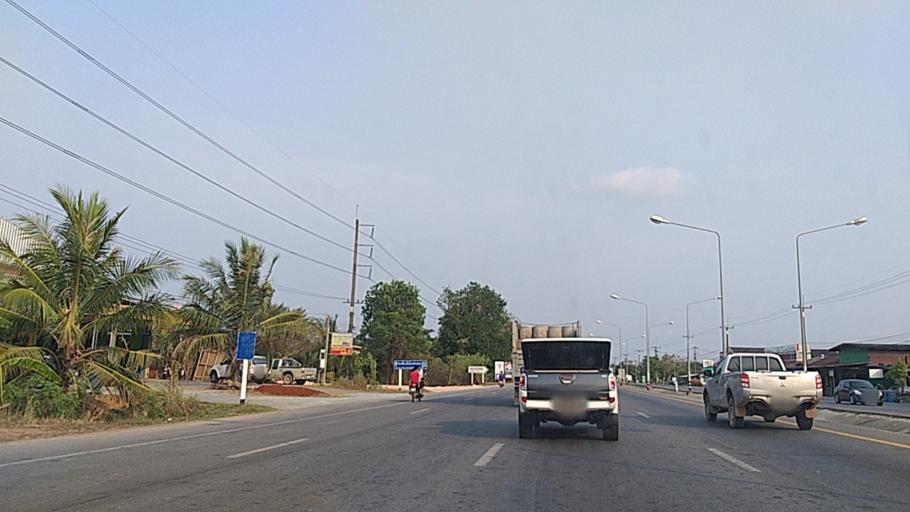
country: TH
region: Chanthaburi
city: Khlung
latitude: 12.4587
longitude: 102.2327
